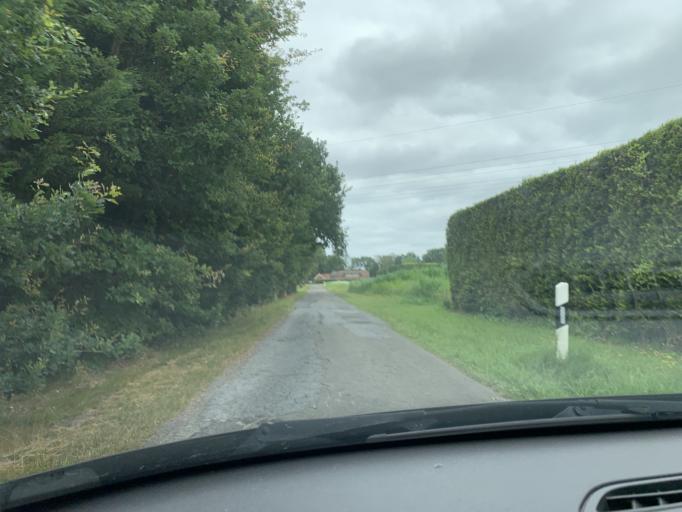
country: DE
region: Lower Saxony
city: Westerstede
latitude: 53.2226
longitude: 7.9659
